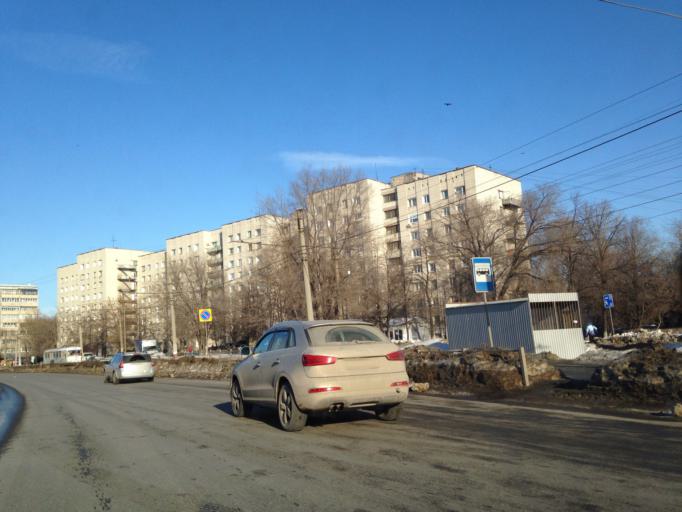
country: RU
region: Ulyanovsk
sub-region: Ulyanovskiy Rayon
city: Ulyanovsk
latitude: 54.3157
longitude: 48.3563
